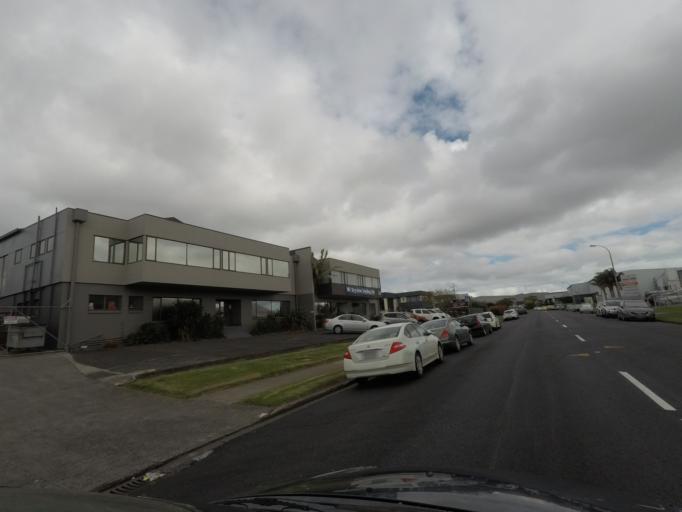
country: NZ
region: Auckland
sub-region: Auckland
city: Tamaki
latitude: -36.9322
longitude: 174.8842
